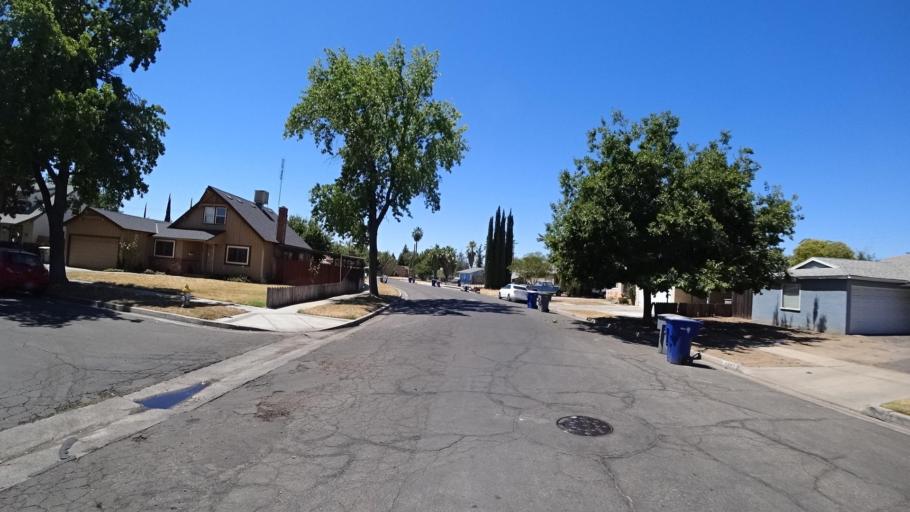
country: US
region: California
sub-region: Fresno County
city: Fresno
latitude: 36.8058
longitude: -119.7840
